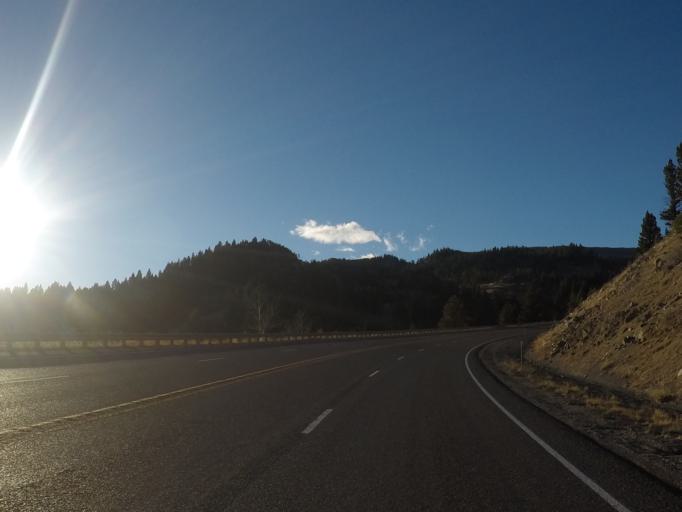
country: US
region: Montana
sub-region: Lewis and Clark County
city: Helena West Side
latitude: 46.5796
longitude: -112.2580
